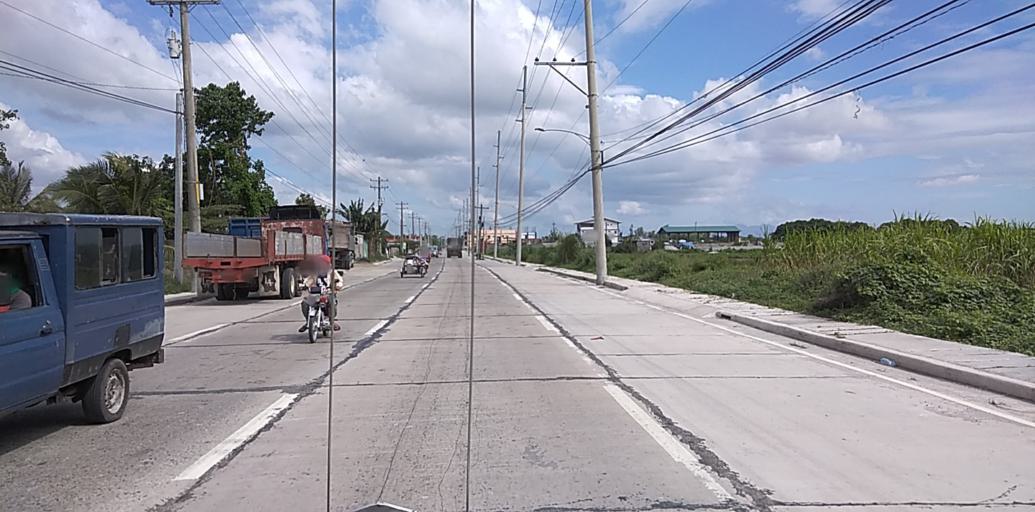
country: PH
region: Central Luzon
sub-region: Province of Pampanga
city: Porac
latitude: 15.0567
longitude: 120.5379
